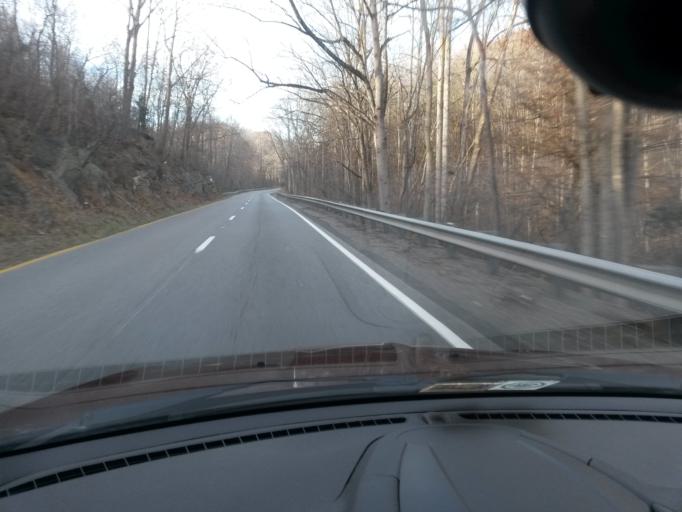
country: US
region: Virginia
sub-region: Botetourt County
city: Fincastle
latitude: 37.5870
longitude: -79.8332
